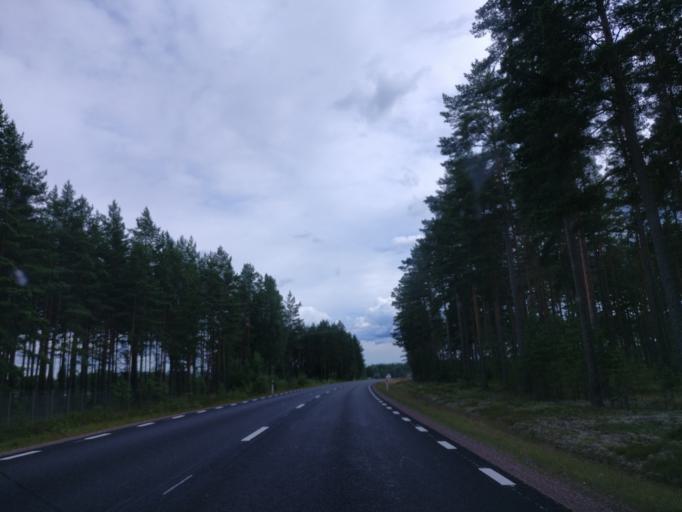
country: SE
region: Vaermland
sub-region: Hagfors Kommun
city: Hagfors
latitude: 60.0403
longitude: 13.5853
